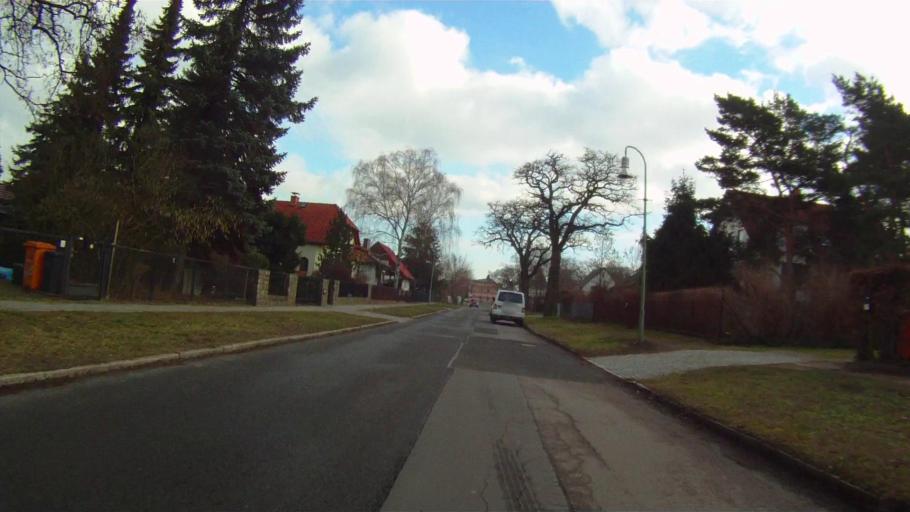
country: DE
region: Berlin
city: Biesdorf
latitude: 52.4940
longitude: 13.5591
